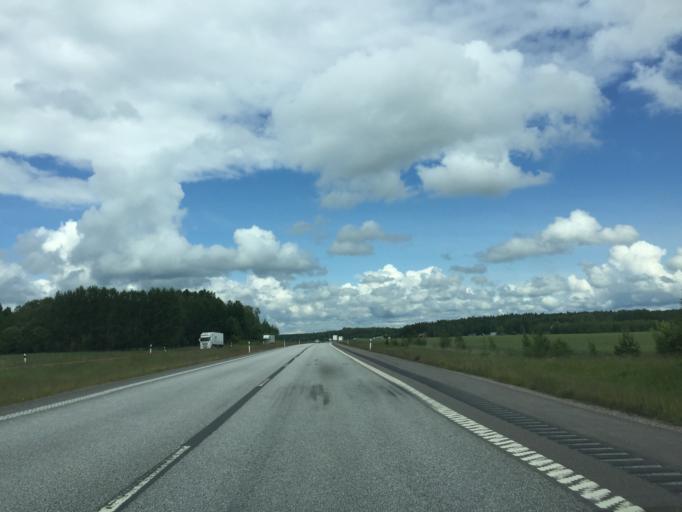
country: SE
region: Vaestmanland
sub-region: Arboga Kommun
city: Arboga
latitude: 59.4496
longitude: 15.8988
